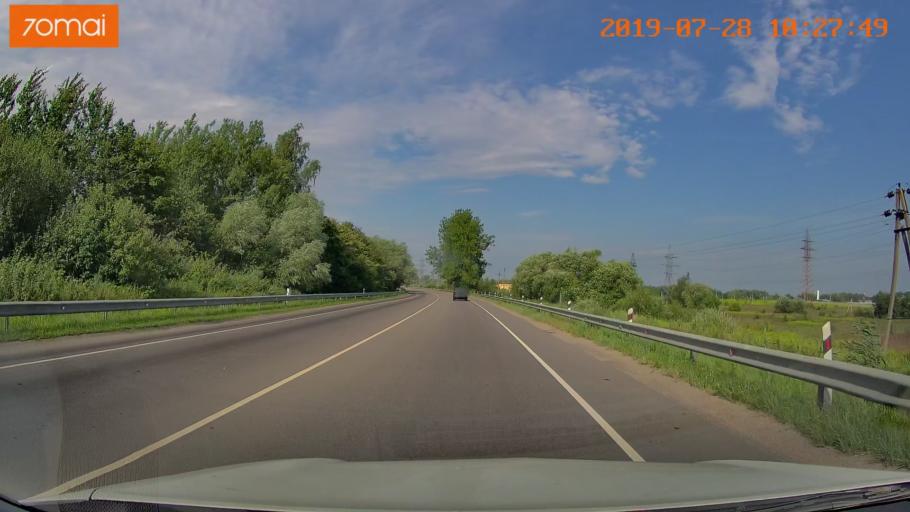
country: RU
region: Kaliningrad
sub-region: Gorod Kaliningrad
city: Kaliningrad
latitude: 54.7716
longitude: 20.5102
